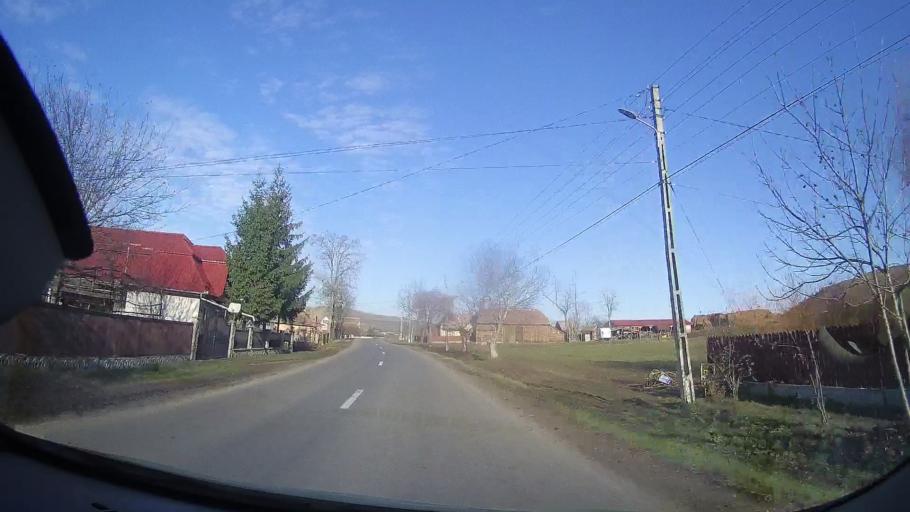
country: RO
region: Mures
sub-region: Comuna Band
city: Band
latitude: 46.5578
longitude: 24.3349
